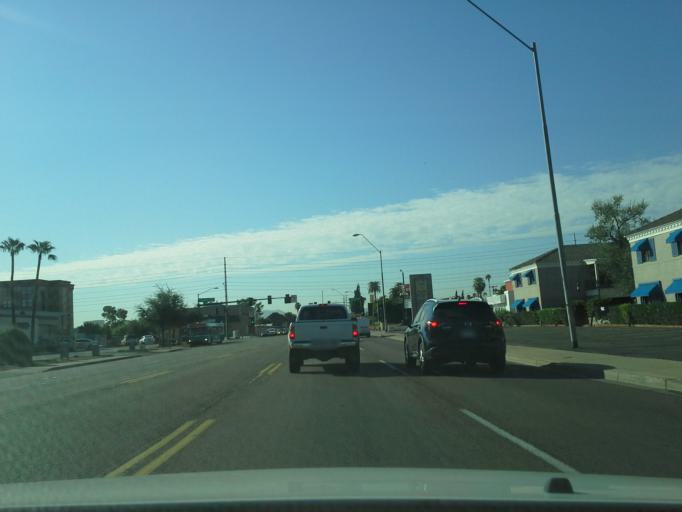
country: US
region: Arizona
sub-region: Maricopa County
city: Phoenix
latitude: 33.4815
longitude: -112.0831
